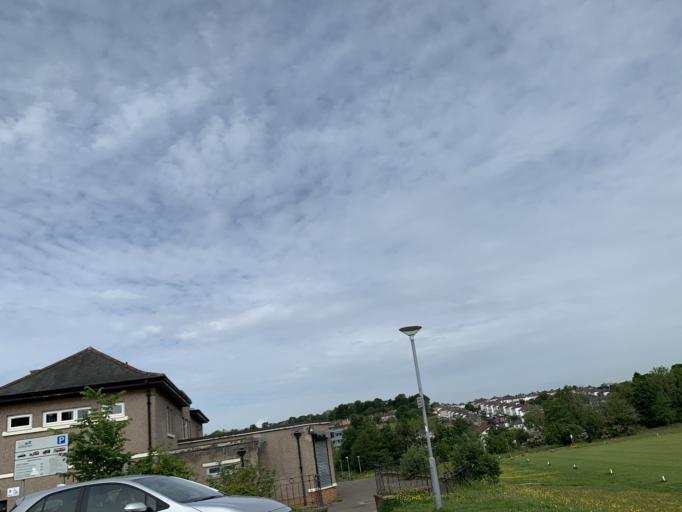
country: GB
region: Scotland
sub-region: East Renfrewshire
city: Giffnock
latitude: 55.8025
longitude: -4.3052
